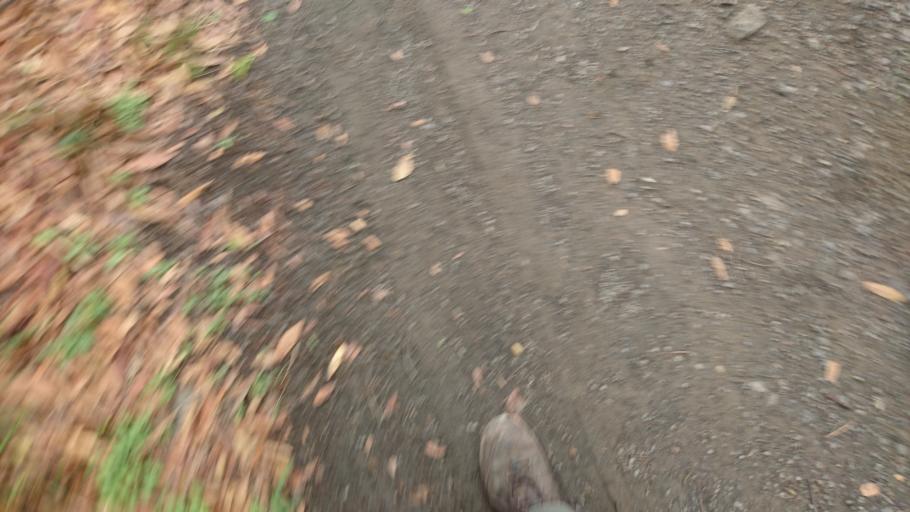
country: MX
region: Nuevo Leon
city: Garza Garcia
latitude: 25.6031
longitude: -100.3404
